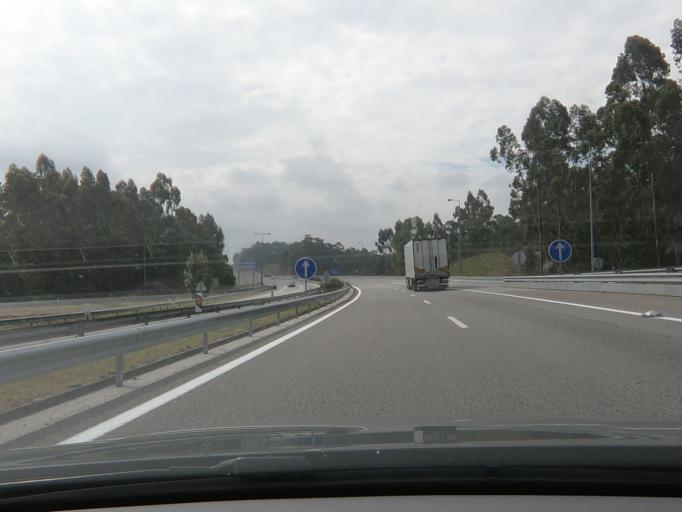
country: PT
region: Aveiro
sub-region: Aveiro
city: Oliveirinha
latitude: 40.6235
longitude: -8.5976
